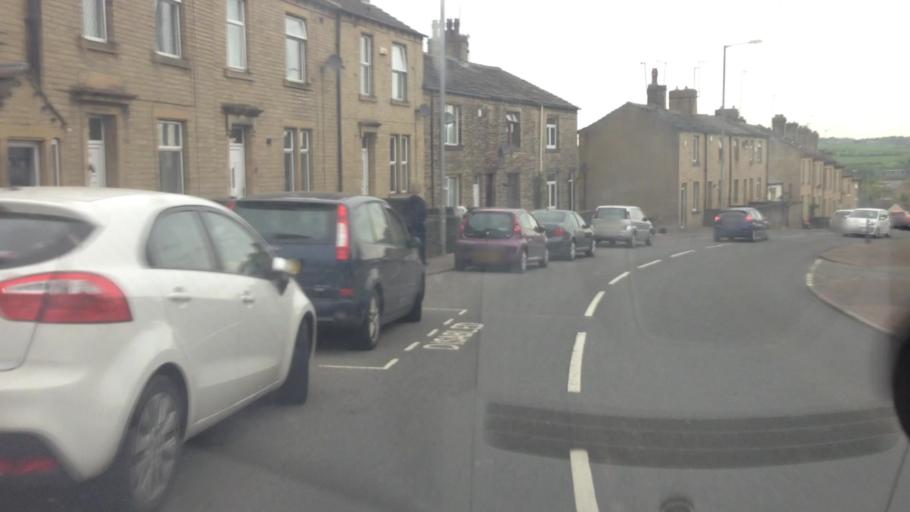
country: GB
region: England
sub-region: Calderdale
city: Brighouse
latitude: 53.6922
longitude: -1.7910
